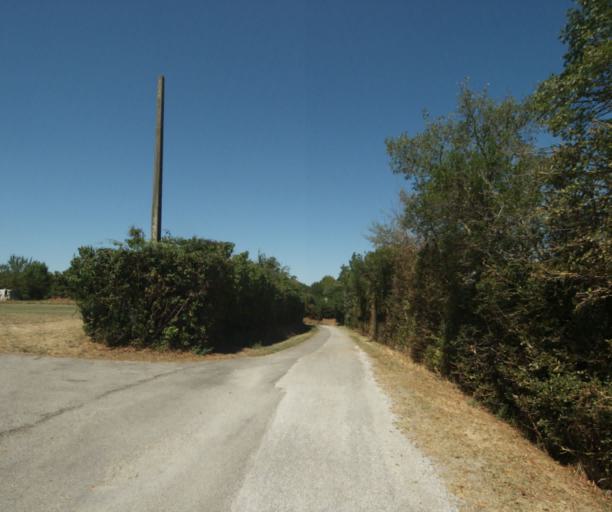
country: FR
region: Midi-Pyrenees
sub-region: Departement de la Haute-Garonne
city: Saint-Felix-Lauragais
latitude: 43.4797
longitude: 1.9239
